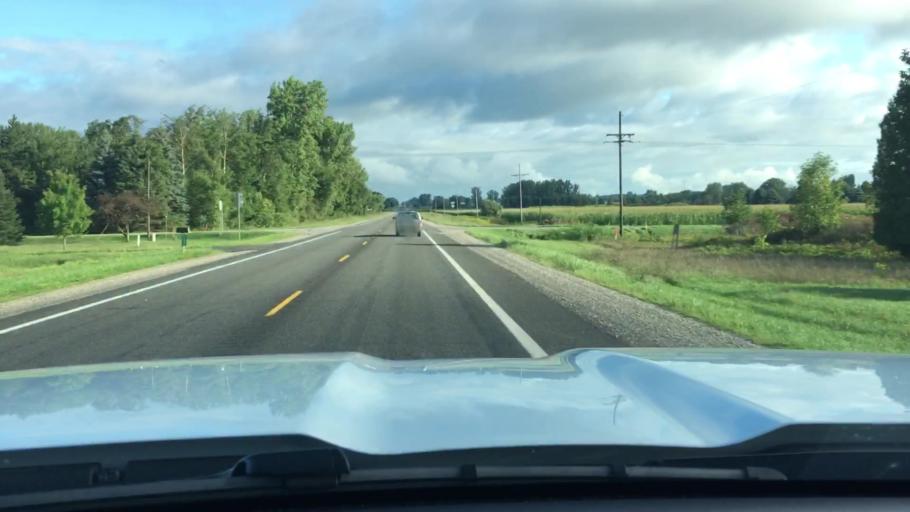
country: US
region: Michigan
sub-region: Tuscola County
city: Caro
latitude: 43.3707
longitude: -83.3831
